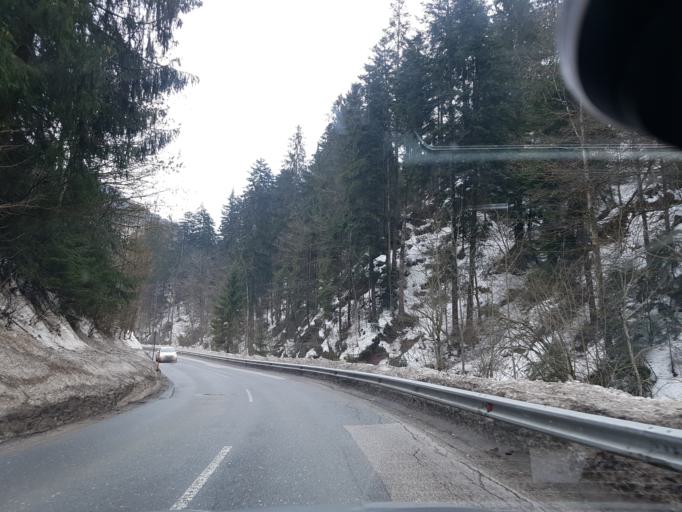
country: AT
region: Tyrol
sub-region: Politischer Bezirk Kufstein
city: Worgl
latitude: 47.4616
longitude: 12.0916
